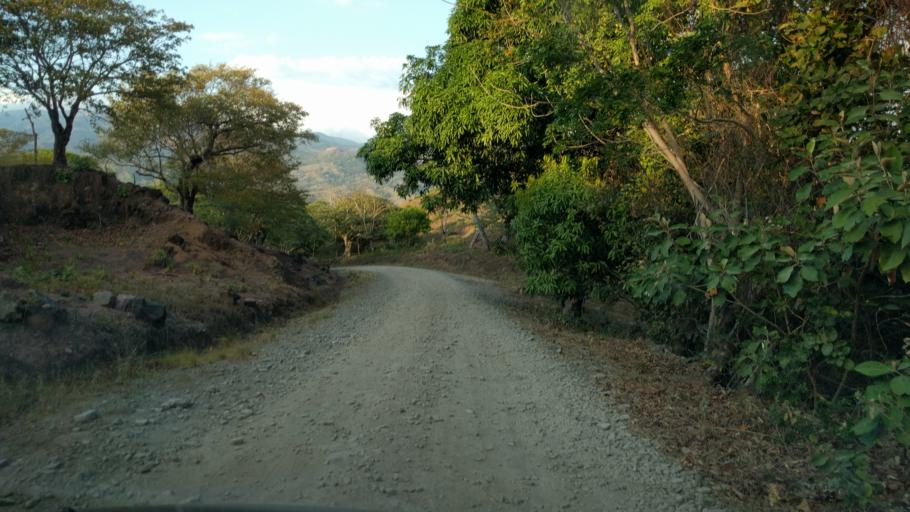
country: CR
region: Puntarenas
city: Esparza
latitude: 10.0276
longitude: -84.6983
